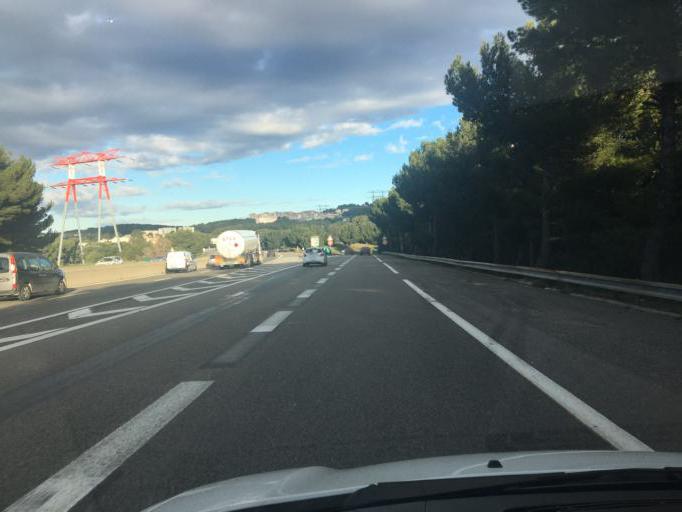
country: FR
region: Provence-Alpes-Cote d'Azur
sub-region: Departement des Bouches-du-Rhone
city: Martigues
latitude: 43.4073
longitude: 5.0385
